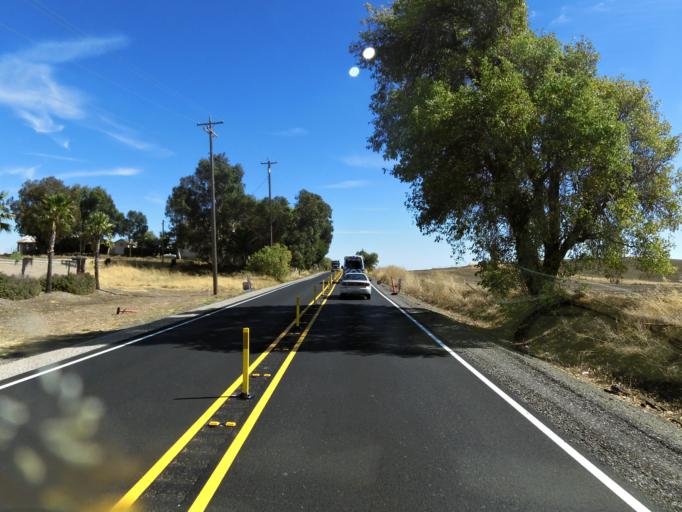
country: US
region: California
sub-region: Solano County
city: Rio Vista
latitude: 38.1744
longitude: -121.7141
